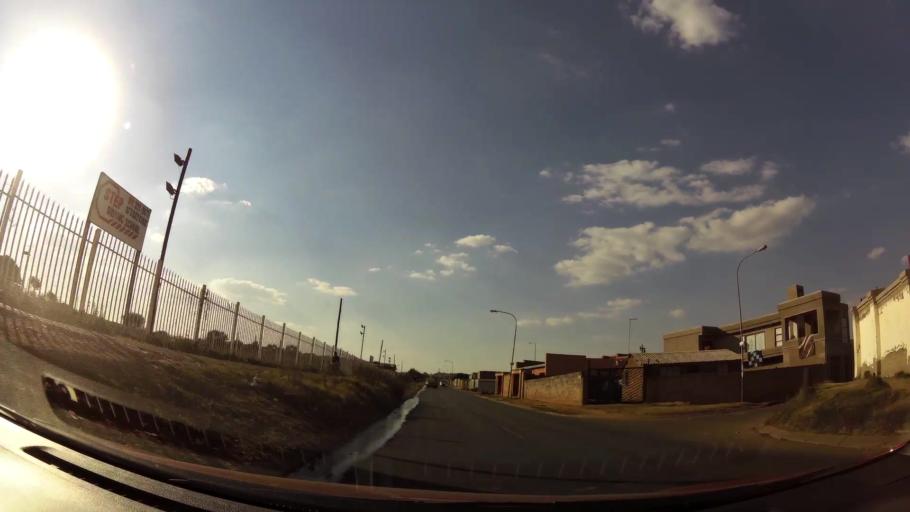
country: ZA
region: Gauteng
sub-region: City of Johannesburg Metropolitan Municipality
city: Roodepoort
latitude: -26.2140
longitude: 27.8761
